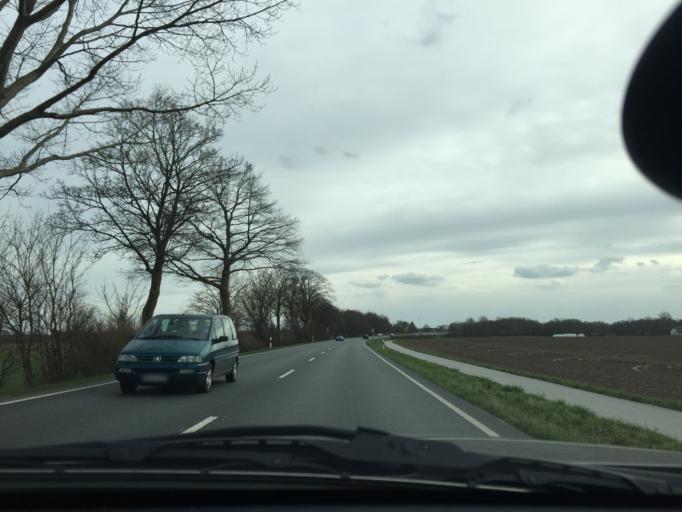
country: DE
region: North Rhine-Westphalia
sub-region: Regierungsbezirk Dusseldorf
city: Goch
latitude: 51.7222
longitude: 6.1586
